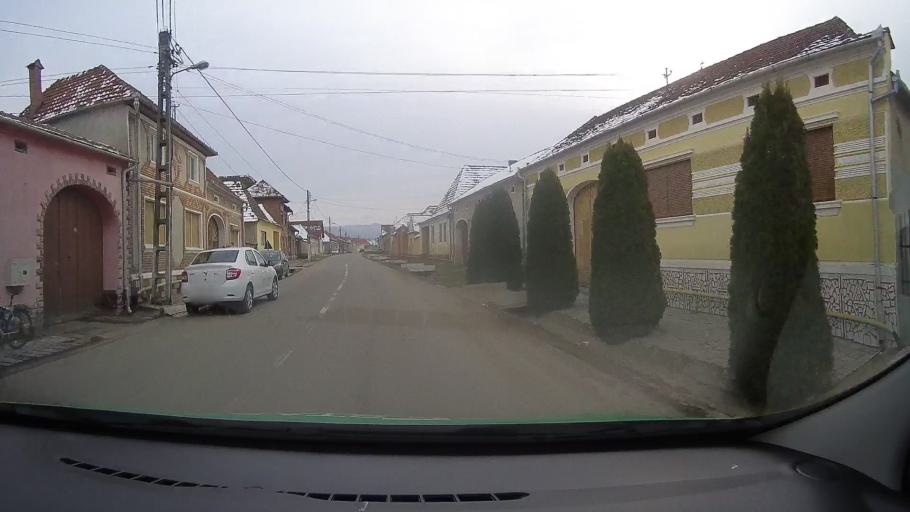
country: RO
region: Hunedoara
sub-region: Comuna Romos
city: Romos
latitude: 45.8461
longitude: 23.2732
